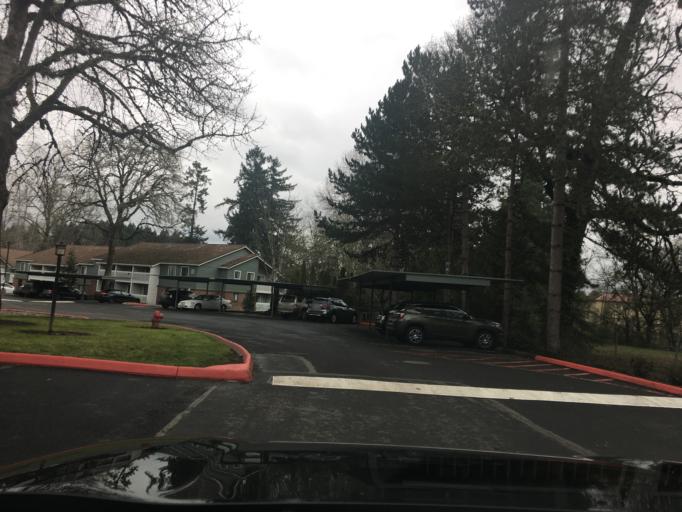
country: US
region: Oregon
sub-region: Washington County
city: Aloha
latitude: 45.4950
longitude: -122.8496
